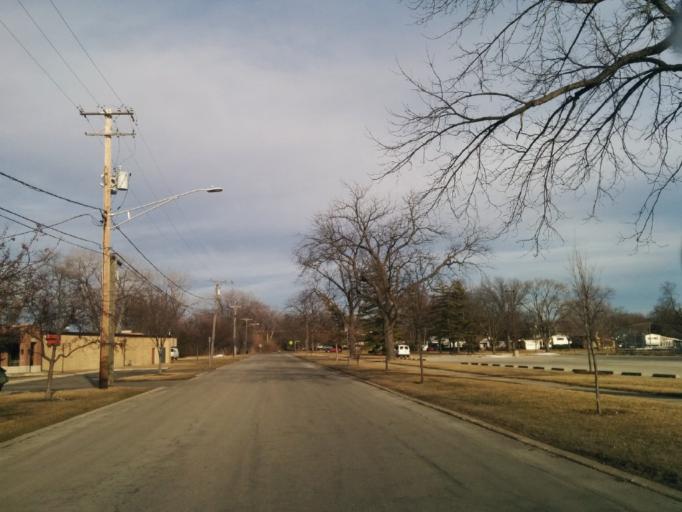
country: US
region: Illinois
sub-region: DuPage County
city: Lombard
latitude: 41.8895
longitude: -88.0057
